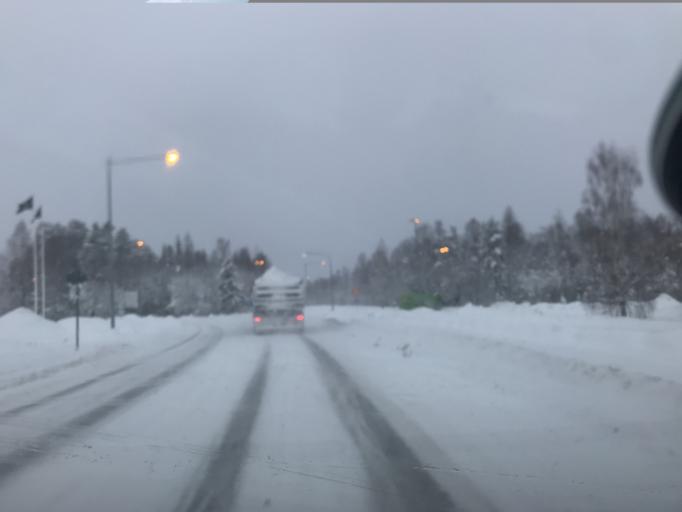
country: SE
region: Norrbotten
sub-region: Lulea Kommun
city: Lulea
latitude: 65.6179
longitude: 22.1305
